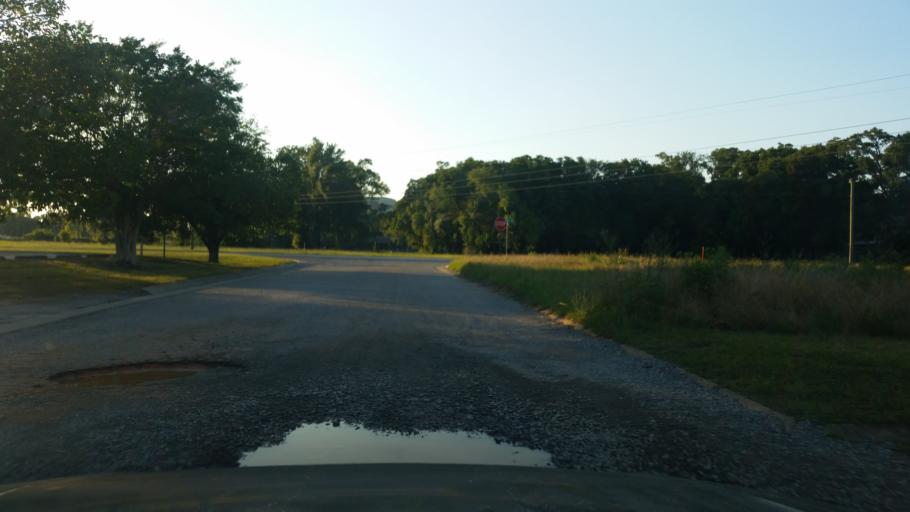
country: US
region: Florida
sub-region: Escambia County
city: Brent
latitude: 30.4675
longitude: -87.2321
